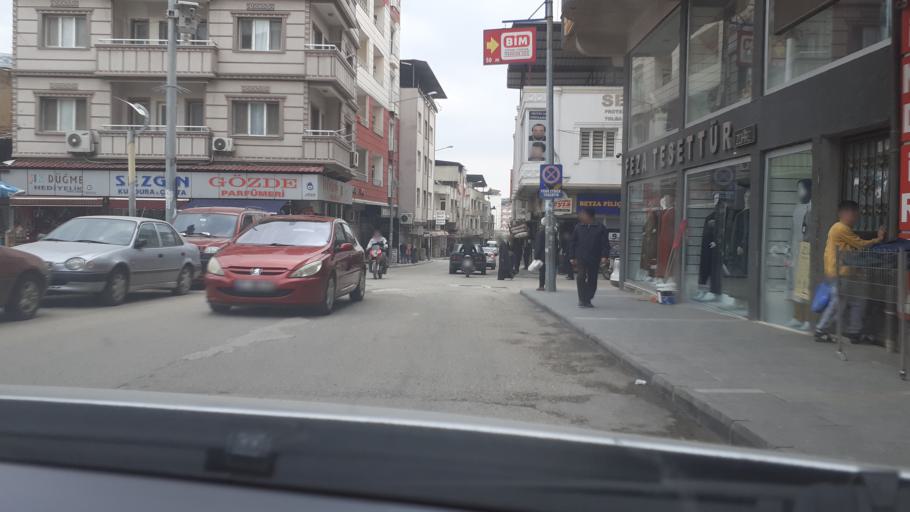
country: TR
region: Hatay
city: Kirikhan
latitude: 36.4977
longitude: 36.3548
